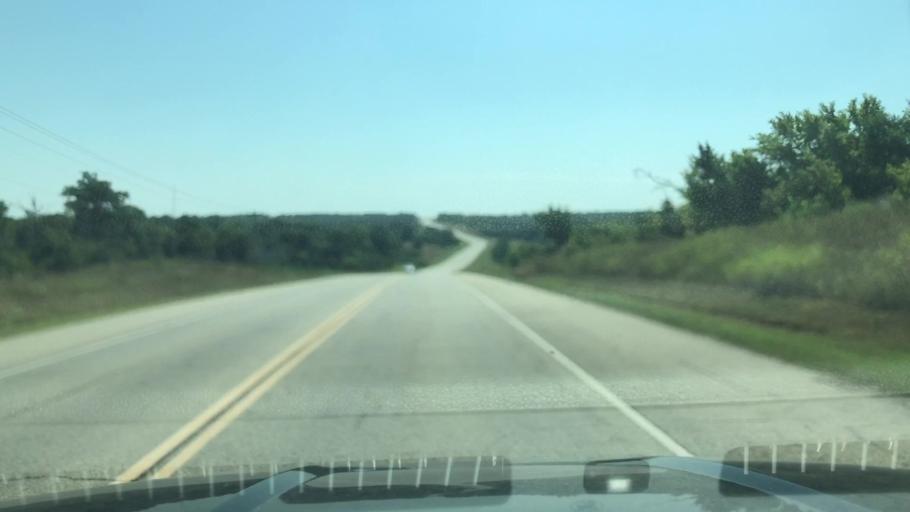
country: US
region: Oklahoma
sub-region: Creek County
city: Mannford
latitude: 36.0031
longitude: -96.4047
